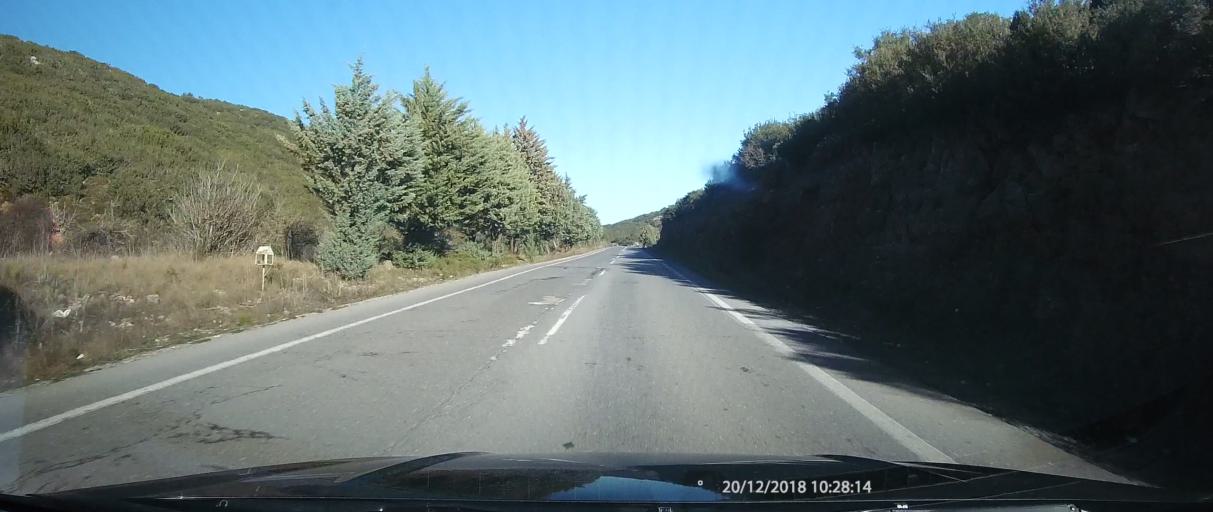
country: GR
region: Peloponnese
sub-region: Nomos Lakonias
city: Kariai
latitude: 37.2581
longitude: 22.4363
